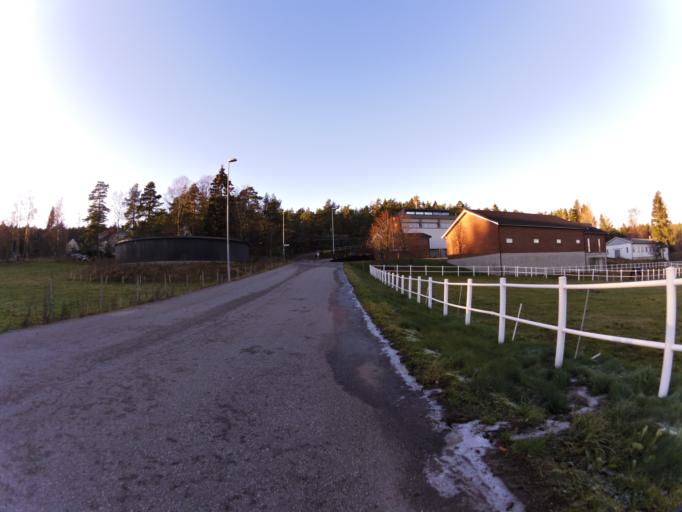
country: NO
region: Ostfold
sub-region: Fredrikstad
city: Fredrikstad
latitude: 59.2444
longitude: 10.9669
